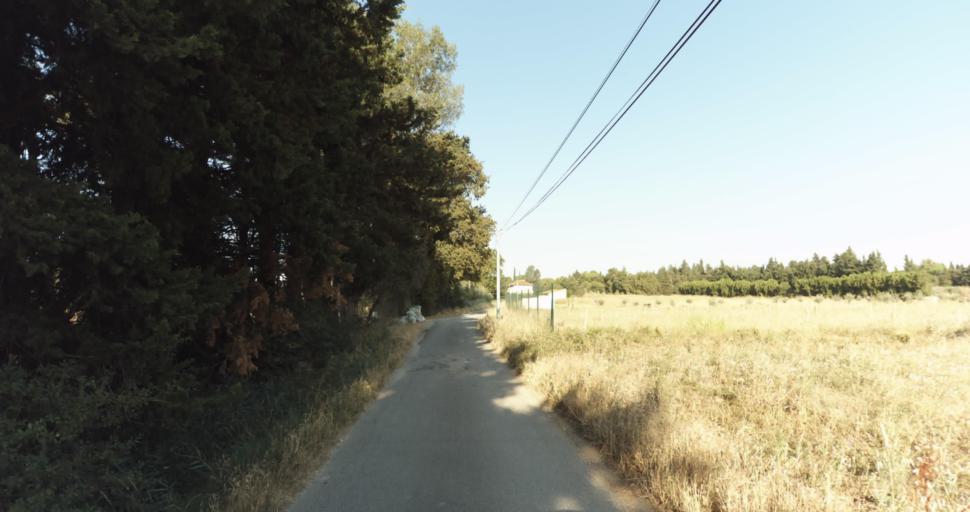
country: FR
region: Provence-Alpes-Cote d'Azur
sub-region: Departement du Vaucluse
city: Monteux
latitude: 44.0424
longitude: 5.0101
